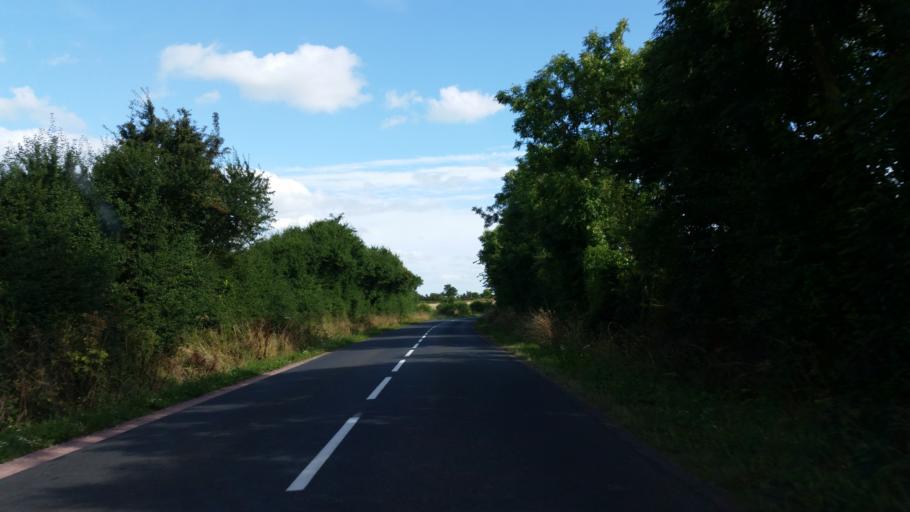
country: FR
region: Lower Normandy
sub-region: Departement de la Manche
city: Sainte-Mere-Eglise
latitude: 49.4527
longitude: -1.2666
